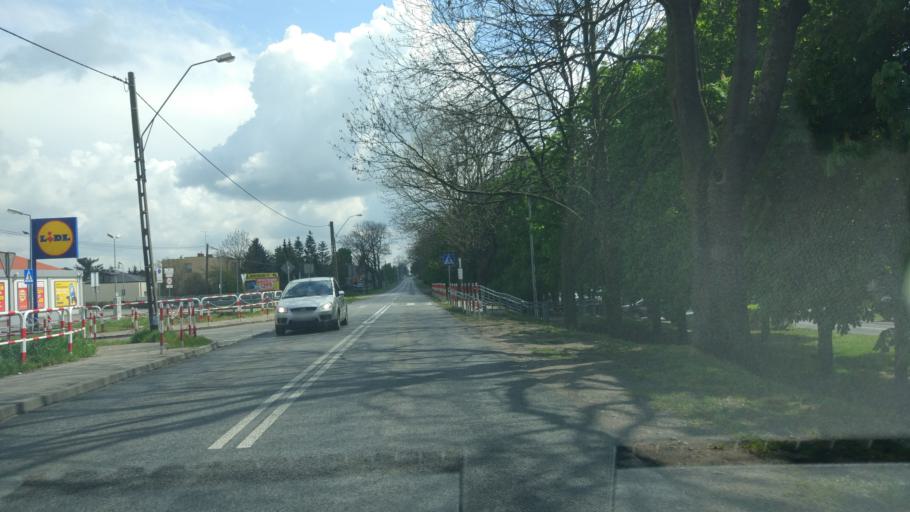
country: PL
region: Lodz Voivodeship
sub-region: Powiat kutnowski
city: Kutno
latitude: 52.2283
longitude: 19.3770
